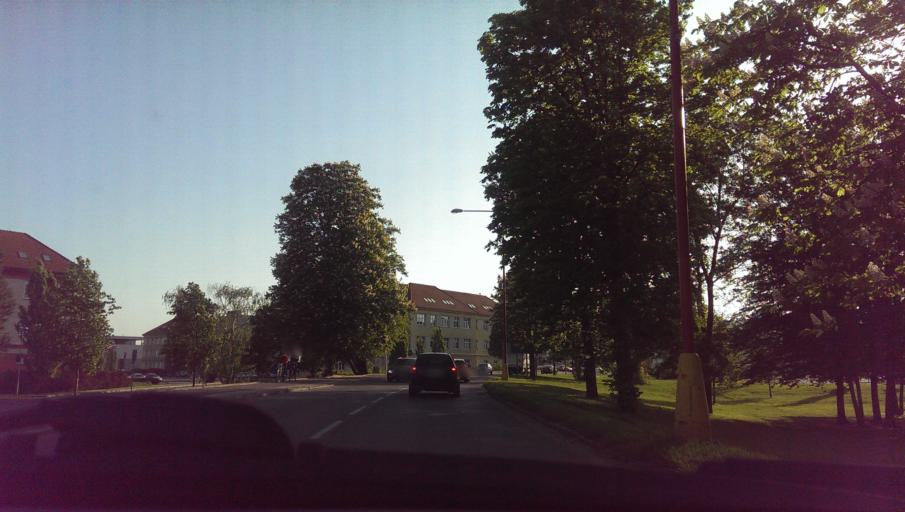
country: CZ
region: Zlin
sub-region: Okres Uherske Hradiste
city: Uherske Hradiste
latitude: 49.0687
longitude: 17.4713
